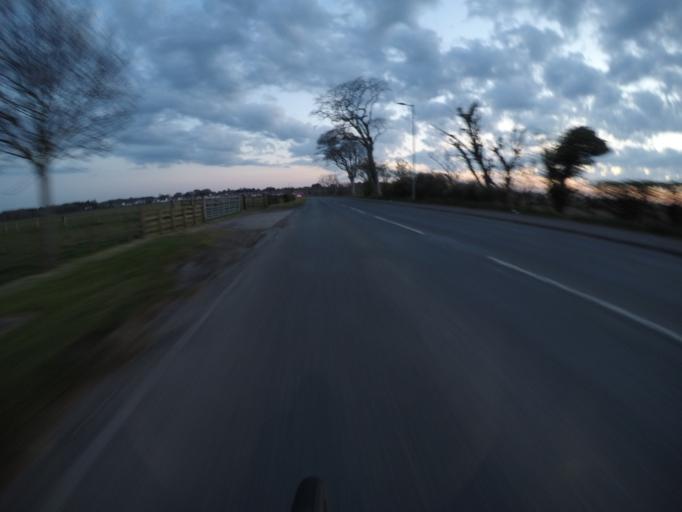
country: GB
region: Scotland
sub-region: South Ayrshire
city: Troon
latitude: 55.5481
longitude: -4.6262
